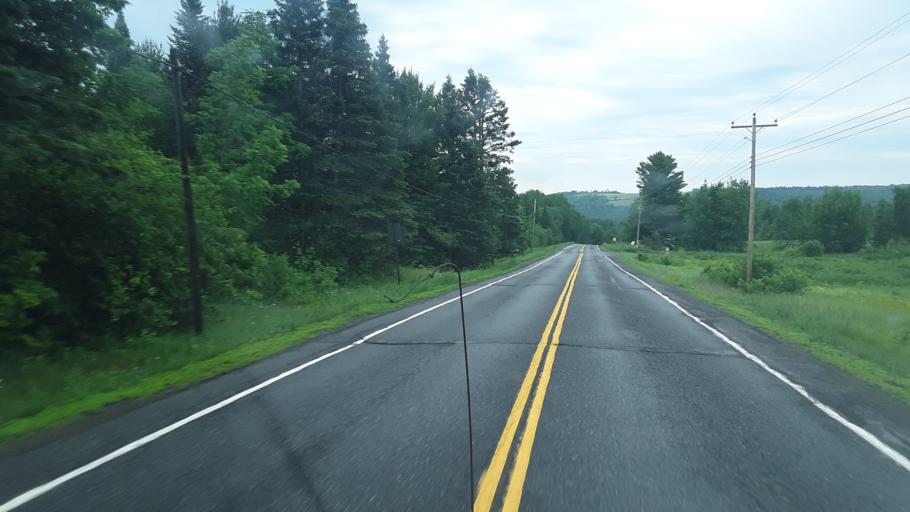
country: US
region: Maine
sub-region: Penobscot County
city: Patten
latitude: 46.0665
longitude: -68.4385
